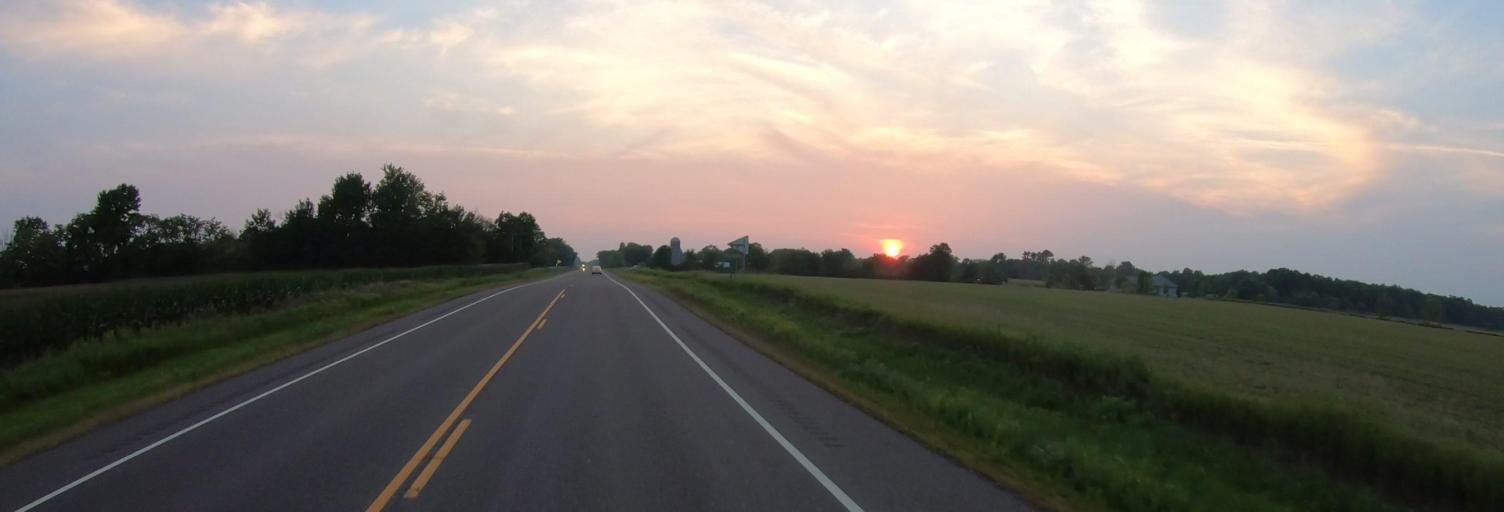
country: US
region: Minnesota
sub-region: Pine County
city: Rock Creek
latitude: 45.7735
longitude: -92.9101
